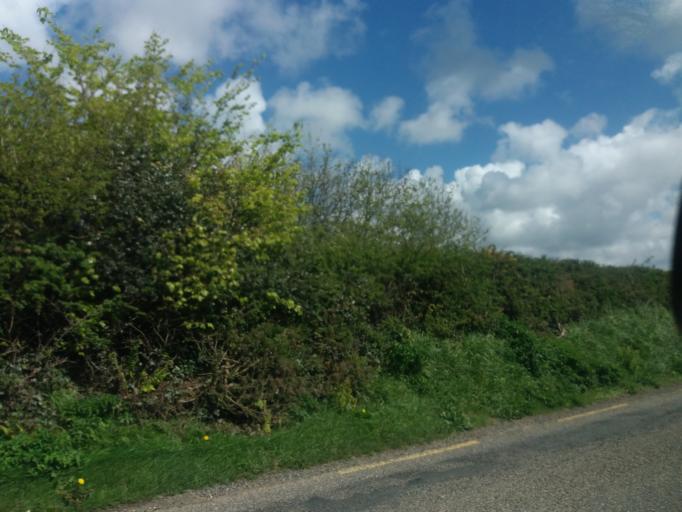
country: IE
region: Leinster
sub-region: Loch Garman
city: Loch Garman
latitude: 52.2816
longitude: -6.7039
